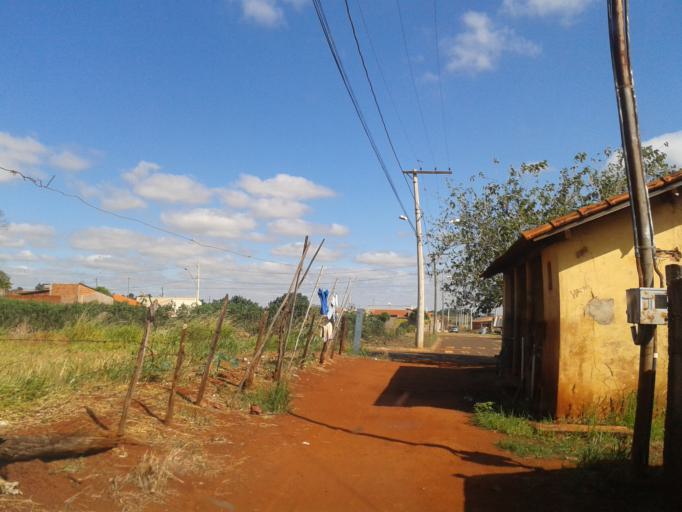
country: BR
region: Minas Gerais
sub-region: Centralina
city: Centralina
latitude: -18.5872
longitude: -49.2039
